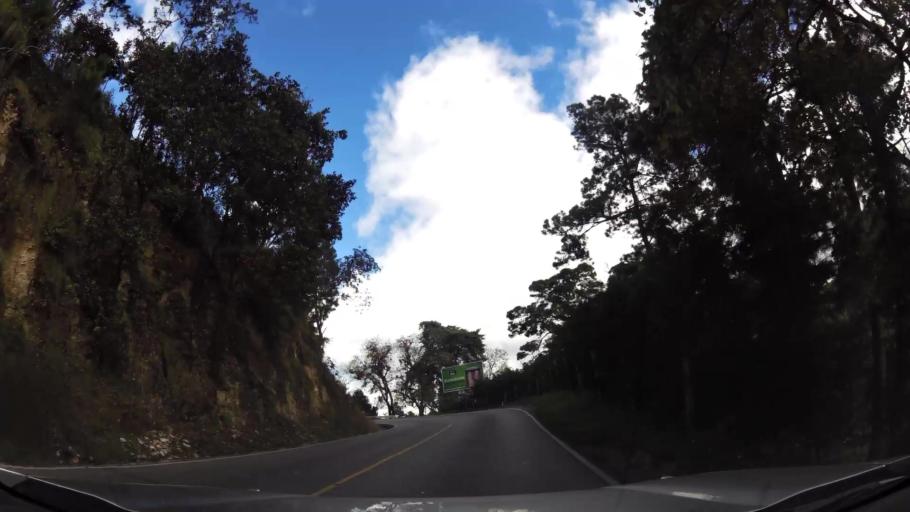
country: GT
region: Quiche
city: Chichicastenango
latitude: 14.9233
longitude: -91.1043
